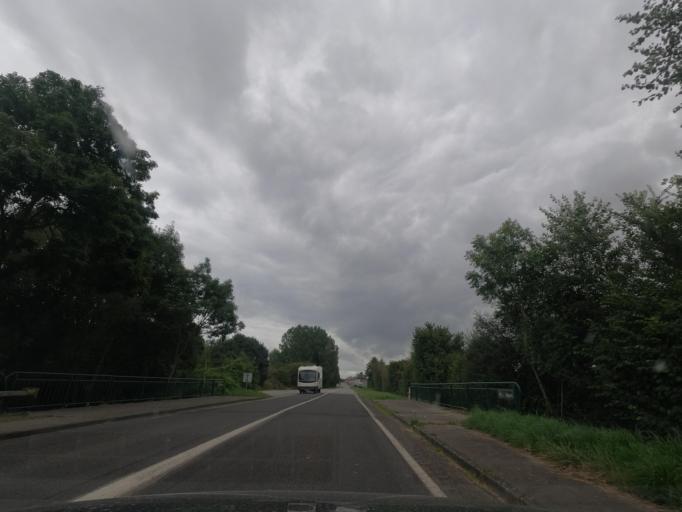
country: FR
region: Lower Normandy
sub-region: Departement de l'Orne
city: Ecouche
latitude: 48.7143
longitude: -0.1283
